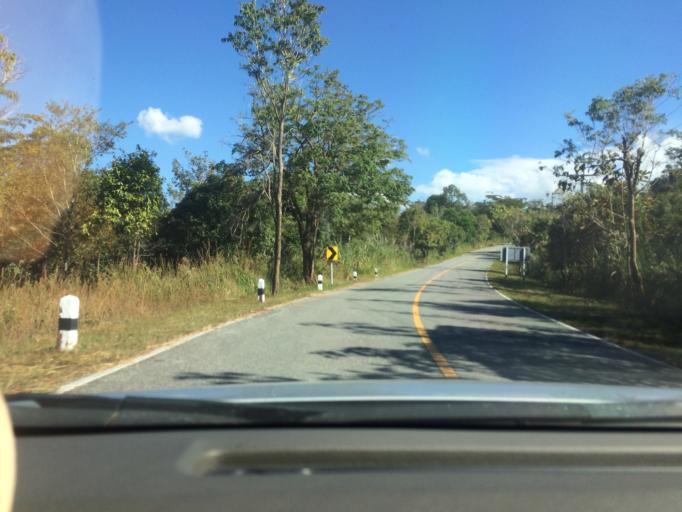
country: TH
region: Phitsanulok
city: Nakhon Thai
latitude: 17.0226
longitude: 100.9825
